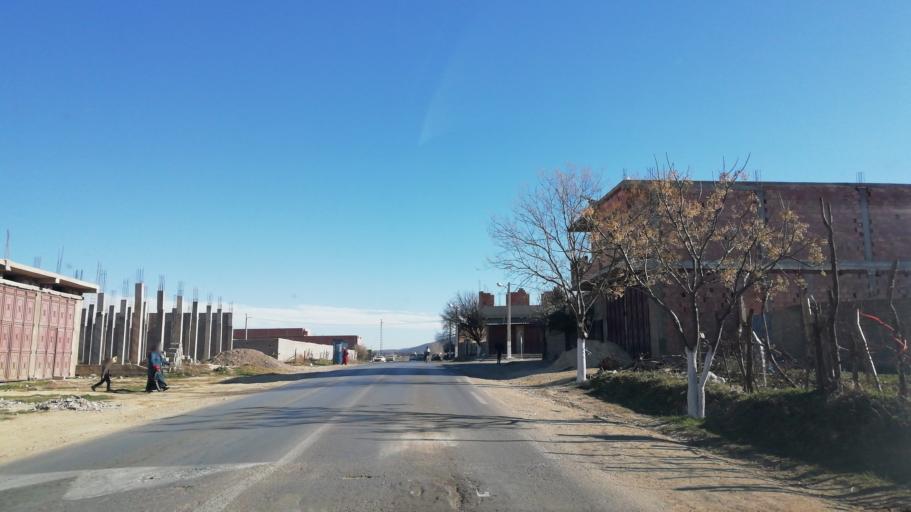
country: DZ
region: Tlemcen
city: Sebdou
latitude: 34.6644
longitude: -1.2894
